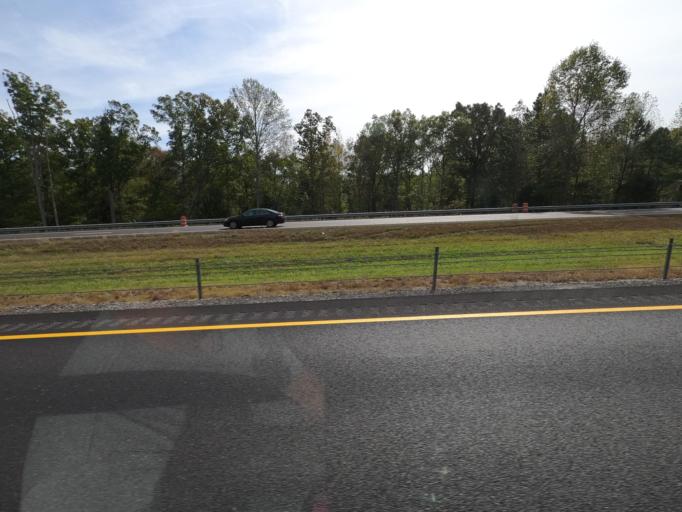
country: US
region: Tennessee
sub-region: Decatur County
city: Parsons
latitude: 35.8336
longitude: -88.0991
